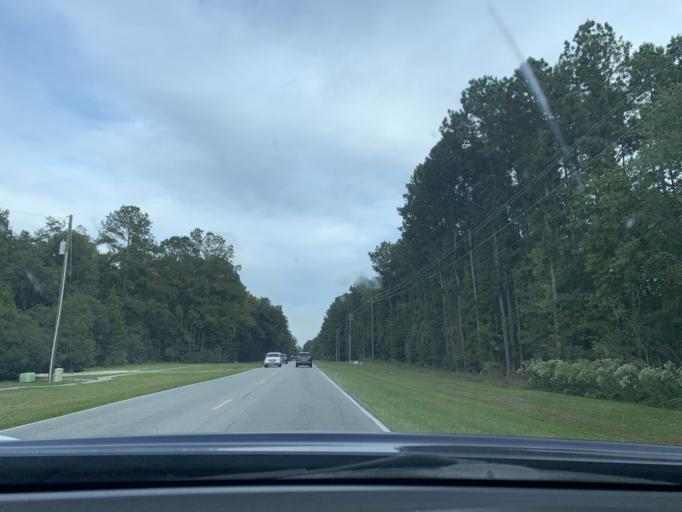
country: US
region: Georgia
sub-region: Chatham County
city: Pooler
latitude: 32.0950
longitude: -81.2665
